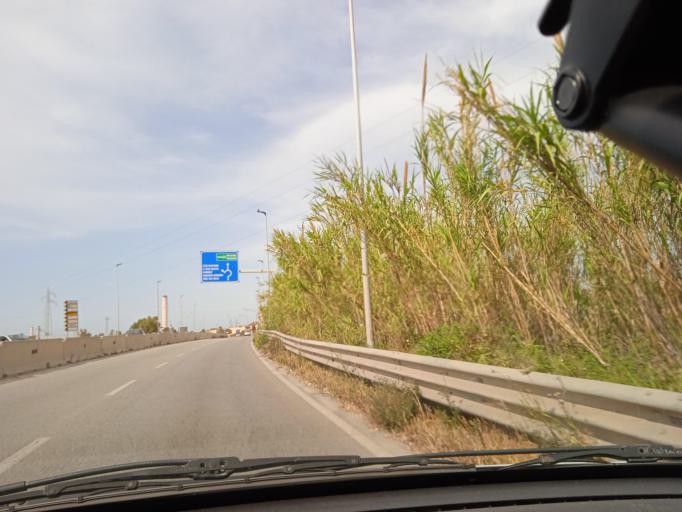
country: IT
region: Sicily
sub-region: Messina
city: San Filippo del Mela
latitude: 38.1864
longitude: 15.2713
